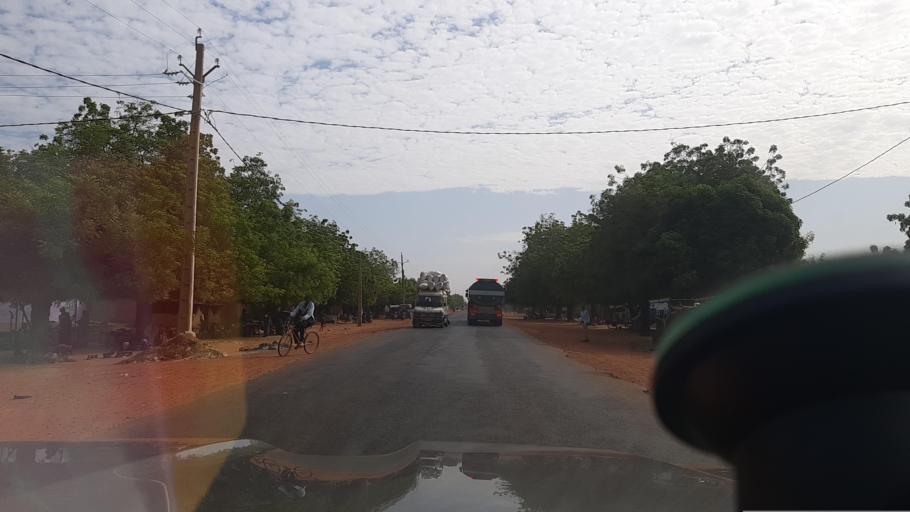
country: ML
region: Segou
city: Segou
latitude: 13.4951
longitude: -6.1712
